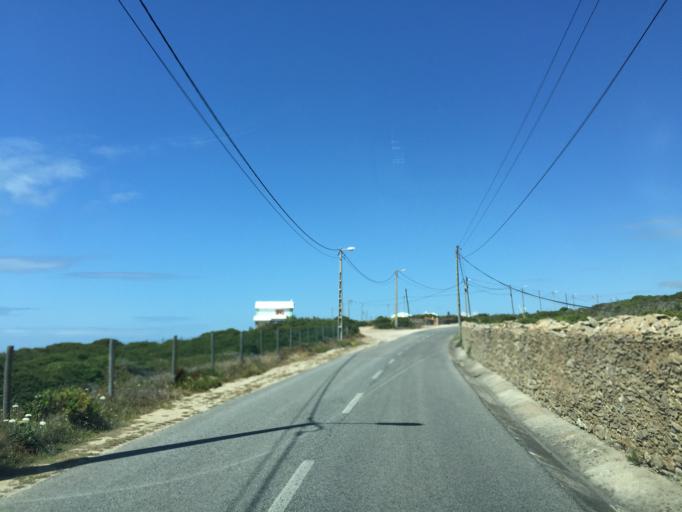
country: PT
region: Lisbon
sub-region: Sintra
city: Colares
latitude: 38.8426
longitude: -9.4605
